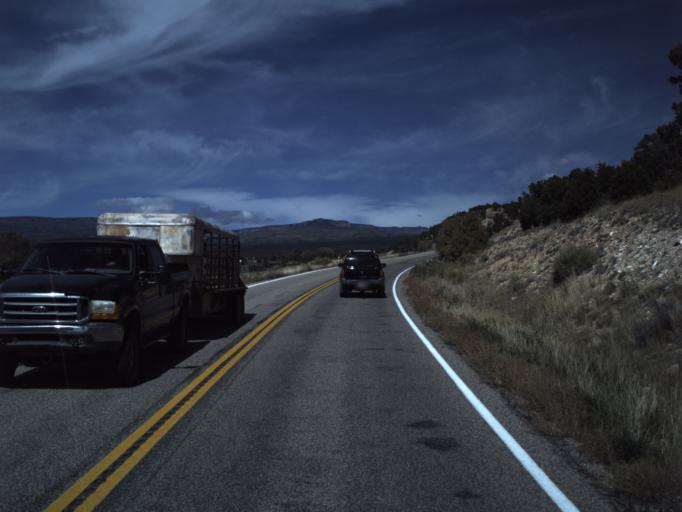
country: US
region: Utah
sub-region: Wayne County
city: Loa
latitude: 37.9335
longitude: -111.4308
